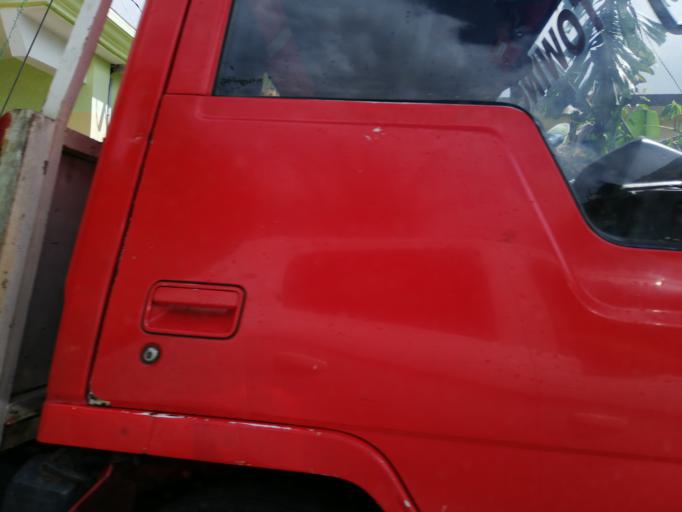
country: MU
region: Moka
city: Moka
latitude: -20.2189
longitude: 57.4705
